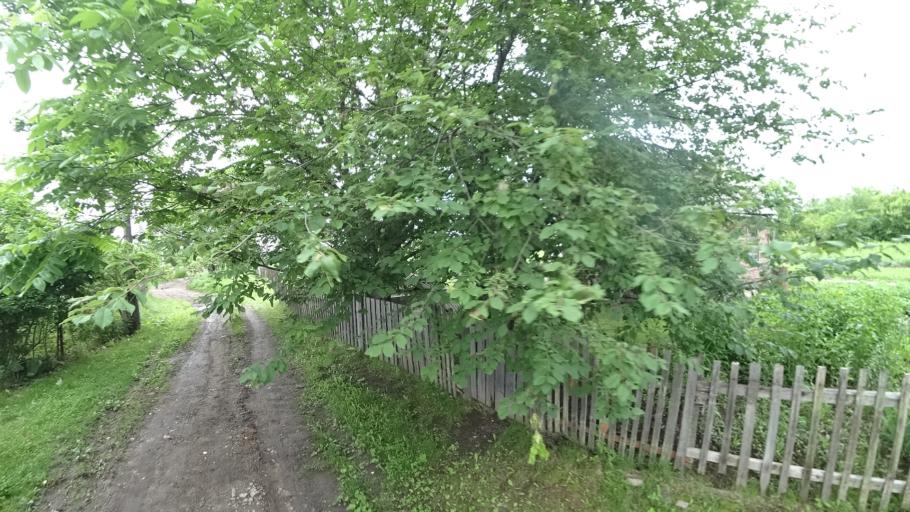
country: RU
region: Primorskiy
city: Novosysoyevka
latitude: 44.2086
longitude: 133.3248
